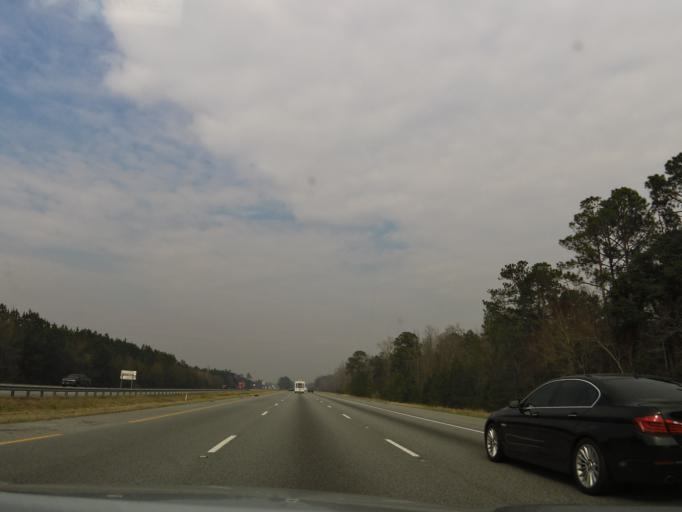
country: US
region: Georgia
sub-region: Liberty County
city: Midway
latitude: 31.6757
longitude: -81.3919
